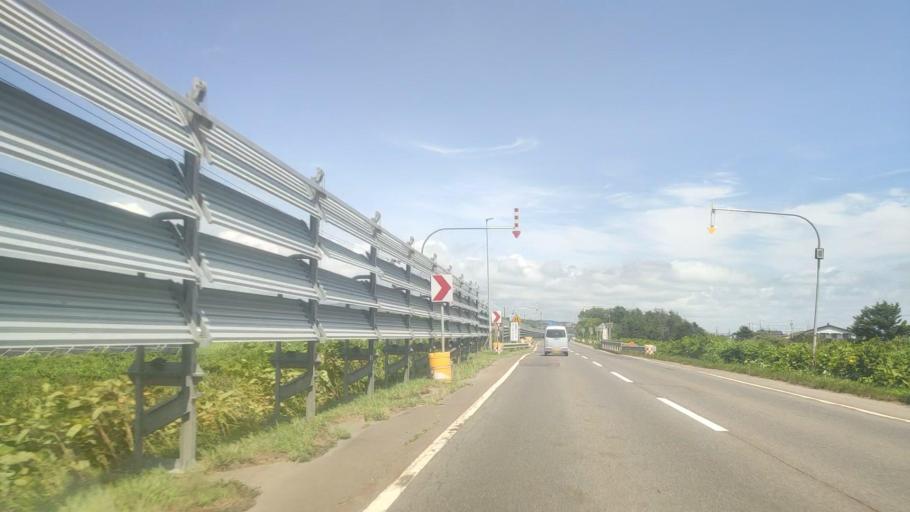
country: JP
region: Hokkaido
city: Nanae
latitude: 42.3027
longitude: 140.2720
